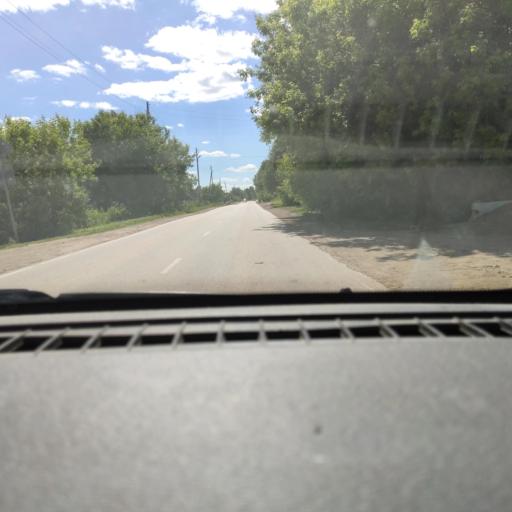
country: RU
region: Perm
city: Chaykovskaya
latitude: 58.1107
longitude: 55.5821
